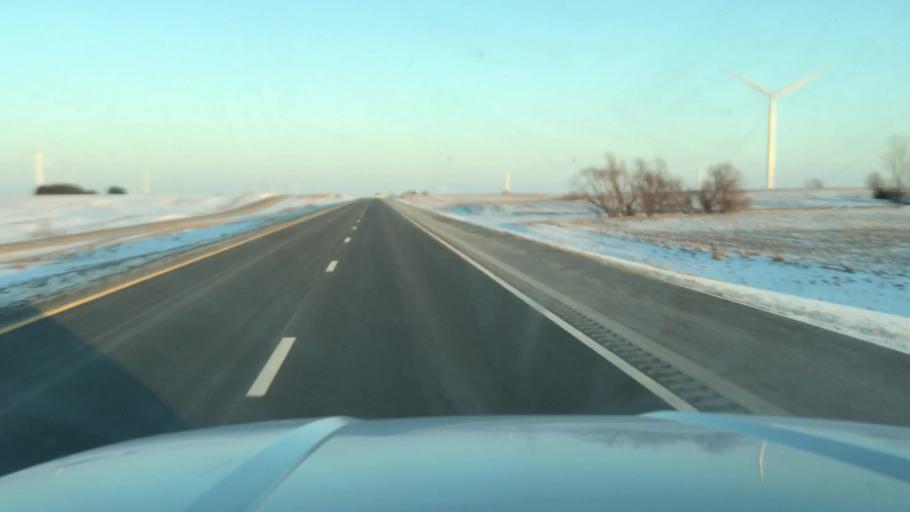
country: US
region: Missouri
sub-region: DeKalb County
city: Maysville
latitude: 39.7617
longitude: -94.4397
